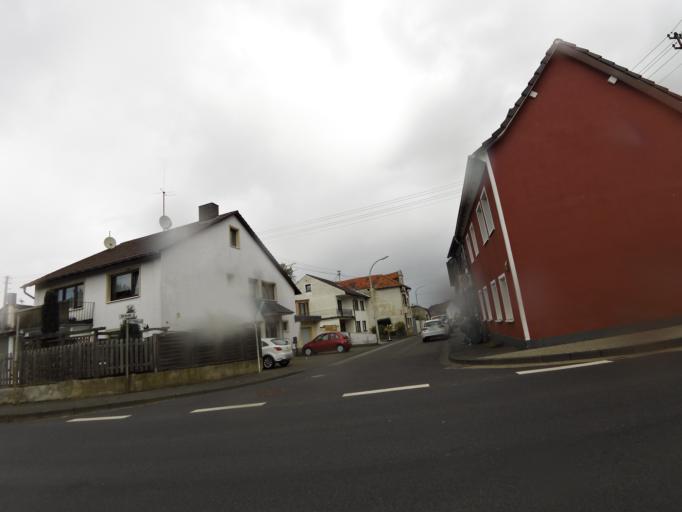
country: DE
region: North Rhine-Westphalia
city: Meckenheim
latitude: 50.5912
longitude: 7.0156
